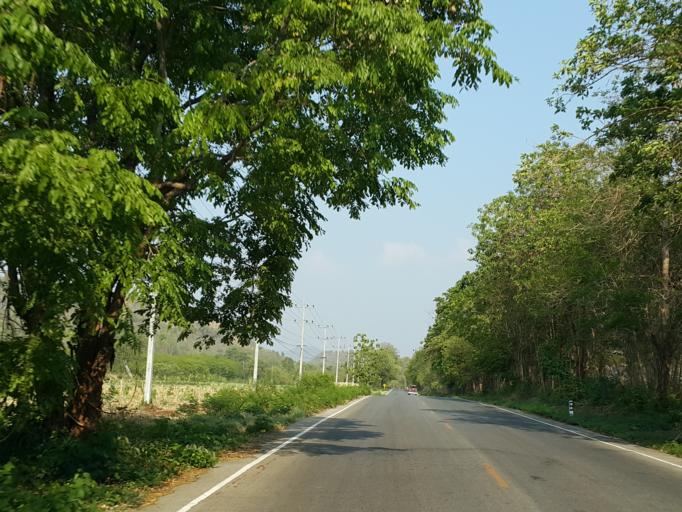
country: TH
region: Kanchanaburi
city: Sai Yok
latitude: 14.2207
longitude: 99.1653
